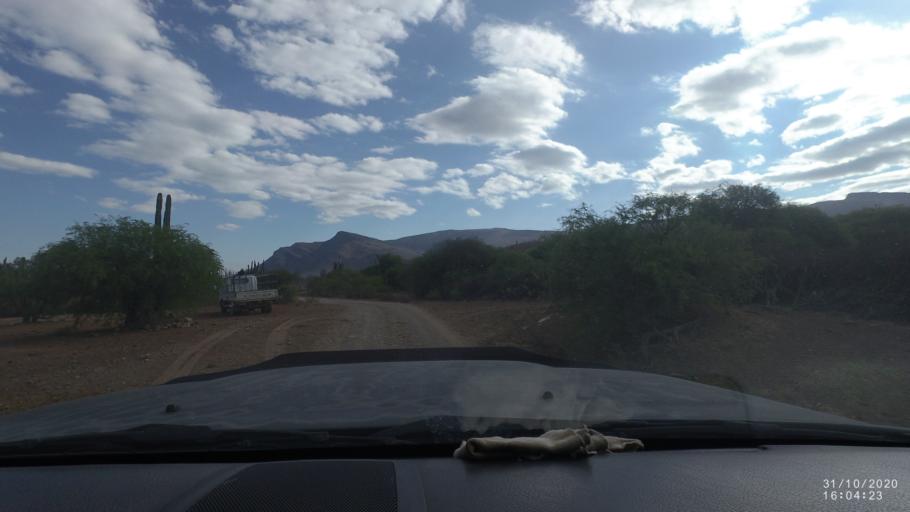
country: BO
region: Chuquisaca
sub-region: Provincia Zudanez
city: Mojocoya
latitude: -18.3590
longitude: -64.6512
